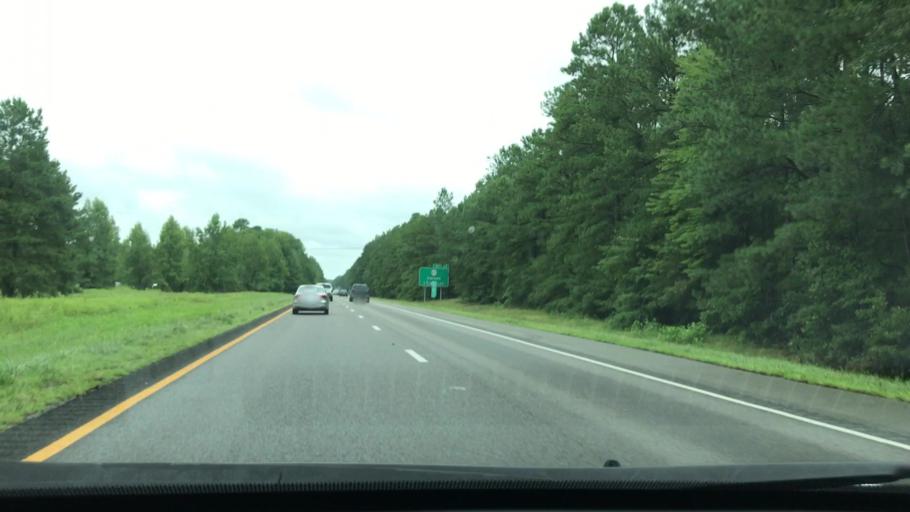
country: US
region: Virginia
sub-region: Sussex County
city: Sussex
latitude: 37.0054
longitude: -77.3918
